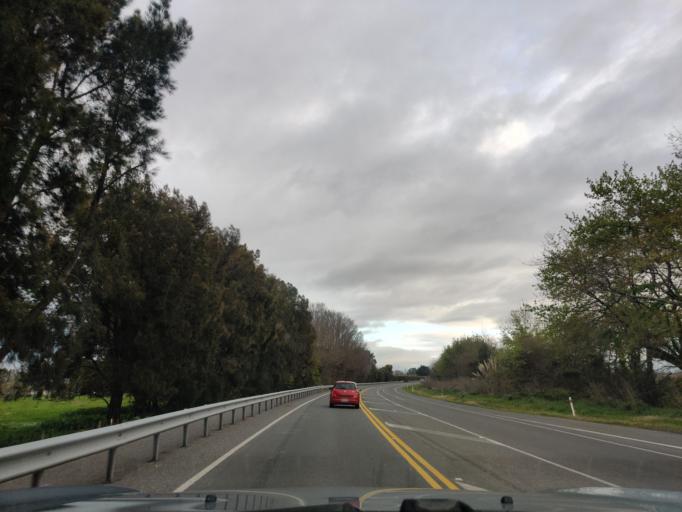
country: NZ
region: Hawke's Bay
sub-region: Napier City
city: Taradale
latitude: -39.5714
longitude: 176.9196
